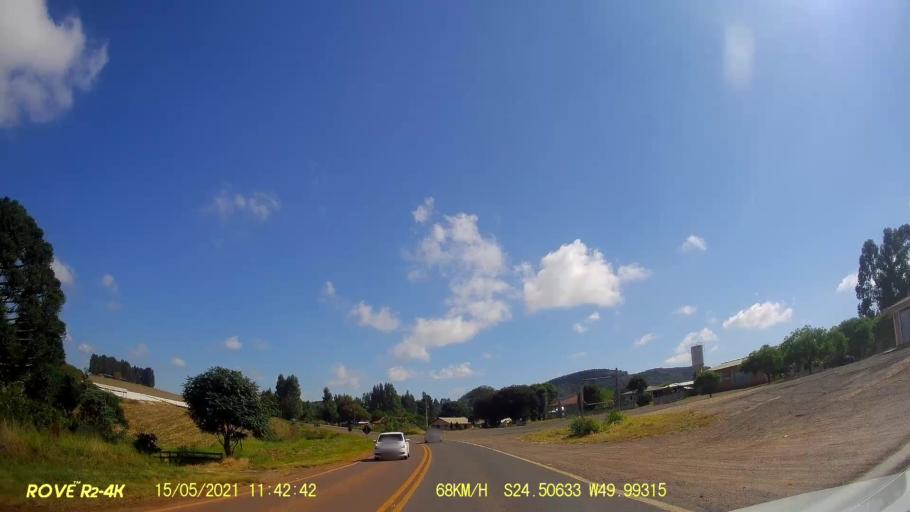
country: BR
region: Parana
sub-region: Pirai Do Sul
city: Pirai do Sul
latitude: -24.5056
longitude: -49.9927
